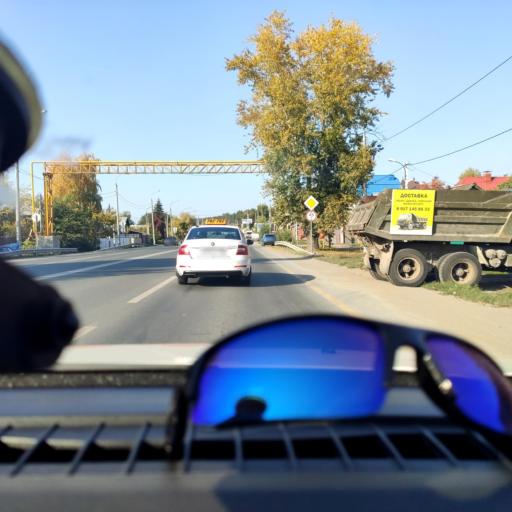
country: RU
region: Samara
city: Volzhskiy
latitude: 53.4280
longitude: 50.1202
